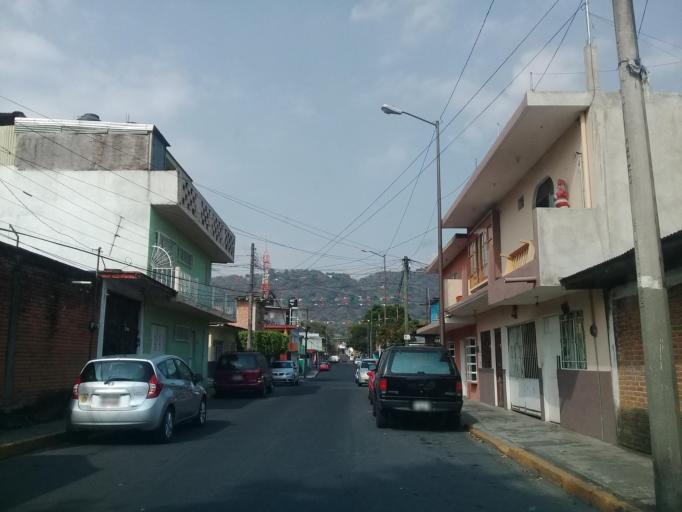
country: MX
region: Veracruz
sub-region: Ixhuatlancillo
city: Union y Progreso
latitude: 18.8679
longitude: -97.1041
